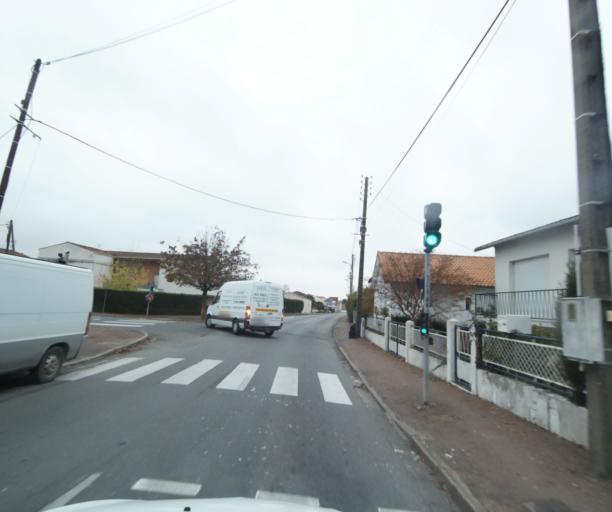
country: FR
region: Poitou-Charentes
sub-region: Departement de la Charente-Maritime
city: Les Gonds
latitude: 45.7366
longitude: -0.6143
